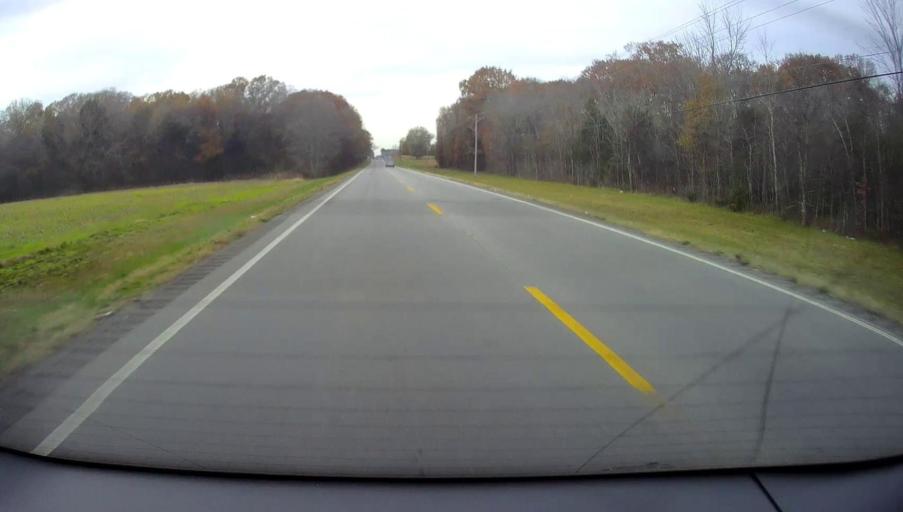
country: US
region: Alabama
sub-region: Morgan County
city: Priceville
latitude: 34.4409
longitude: -86.7480
